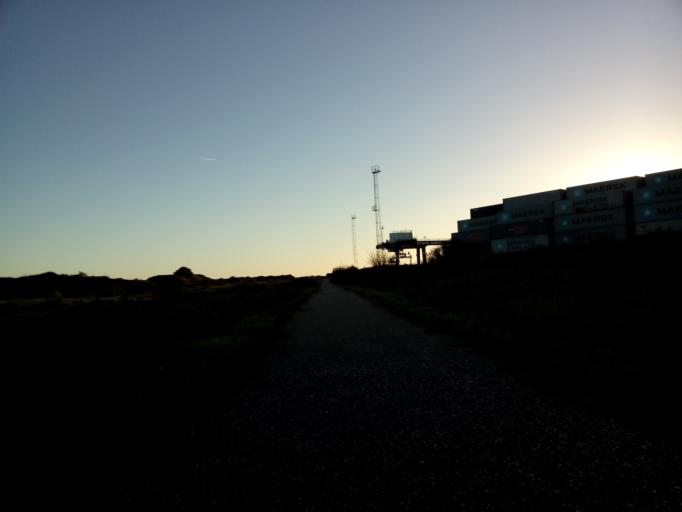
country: GB
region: England
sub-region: Suffolk
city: Felixstowe
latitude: 51.9435
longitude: 1.3279
